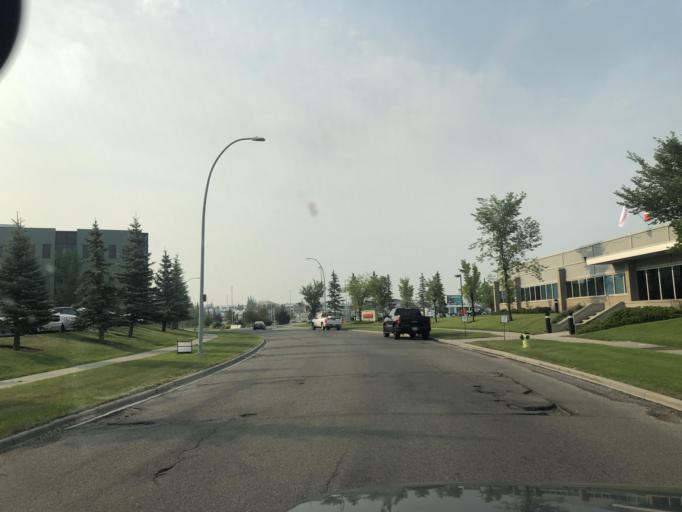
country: CA
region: Alberta
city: Calgary
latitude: 50.9544
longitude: -113.9975
